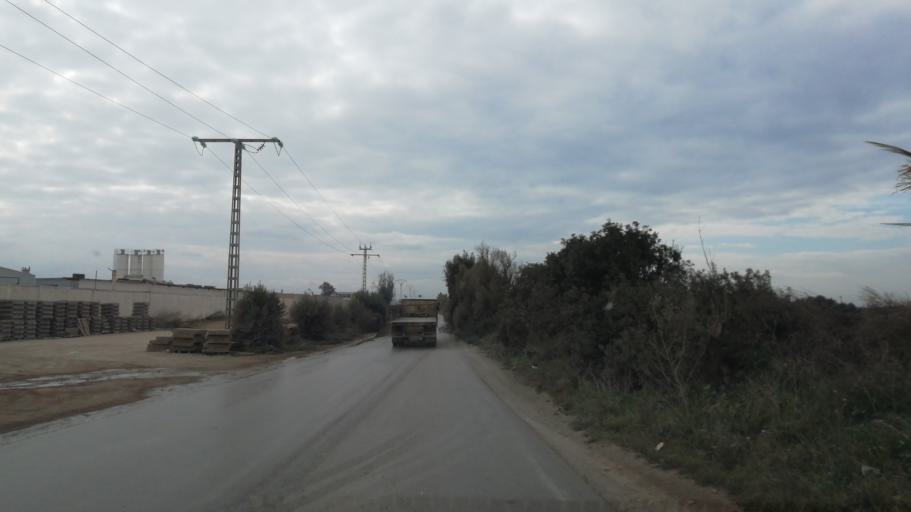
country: DZ
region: Oran
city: Ain el Bya
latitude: 35.7828
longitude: -0.3442
